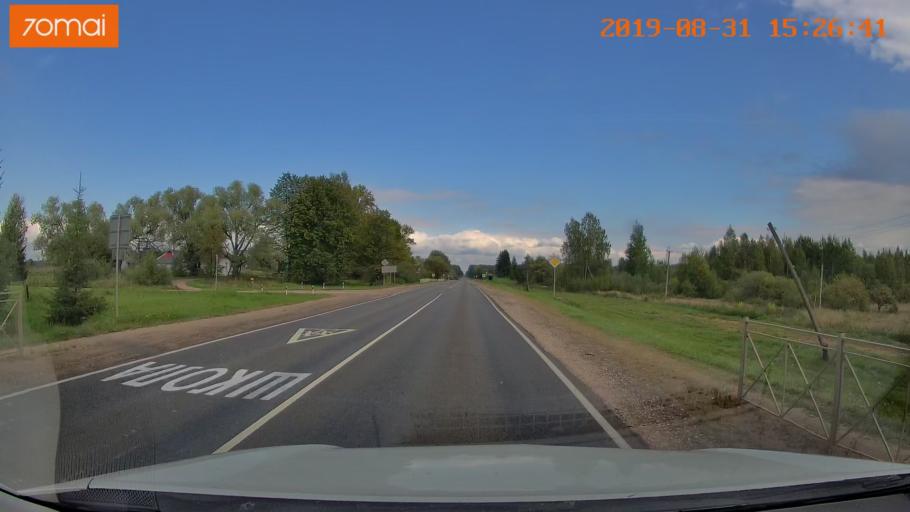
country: RU
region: Kaluga
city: Baryatino
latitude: 54.5516
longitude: 34.5434
